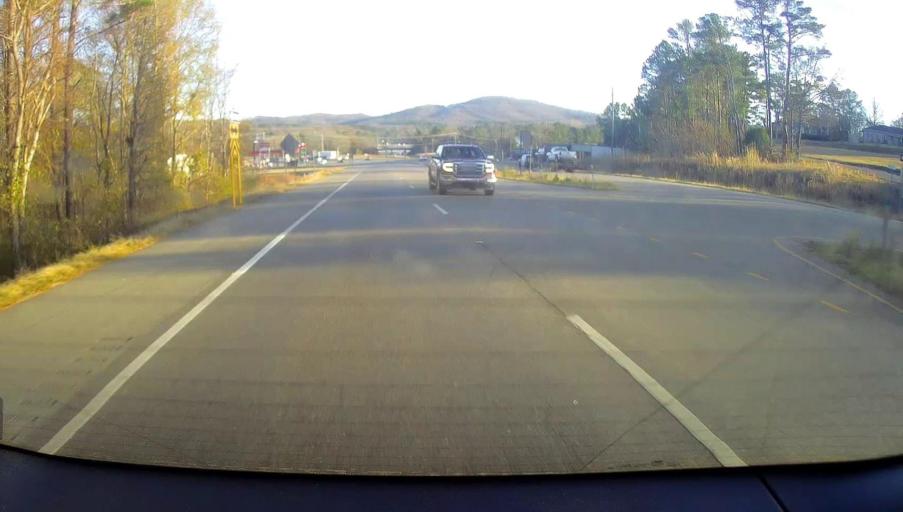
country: US
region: Alabama
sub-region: Calhoun County
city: Saks
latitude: 33.7026
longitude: -85.8309
